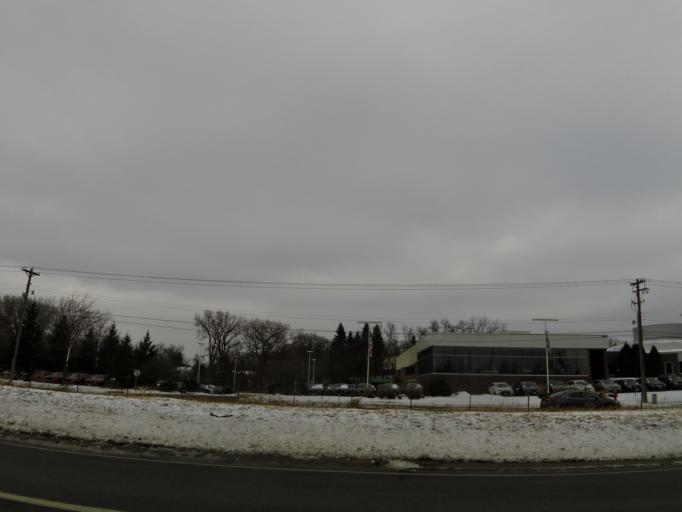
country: US
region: Minnesota
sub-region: Hennepin County
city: Minnetonka Mills
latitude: 44.9712
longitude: -93.4531
